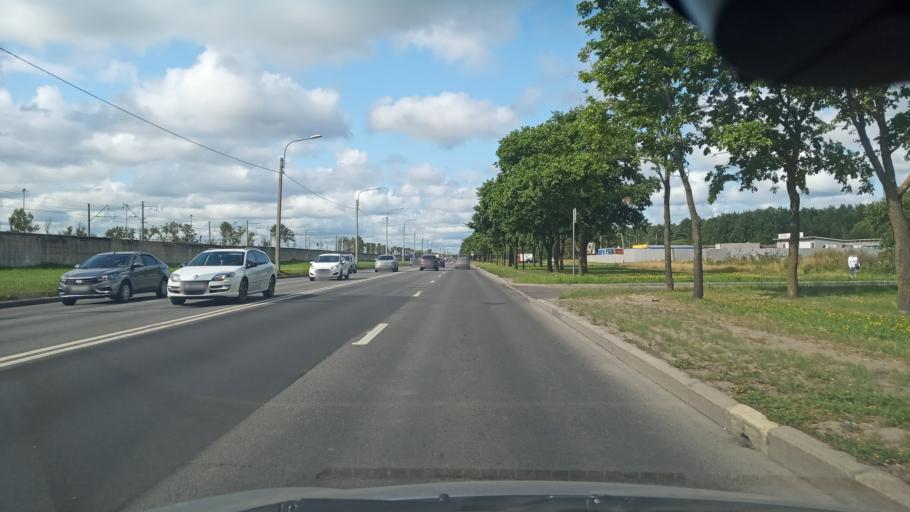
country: RU
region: St.-Petersburg
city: Dachnoye
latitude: 59.8301
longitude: 30.2449
